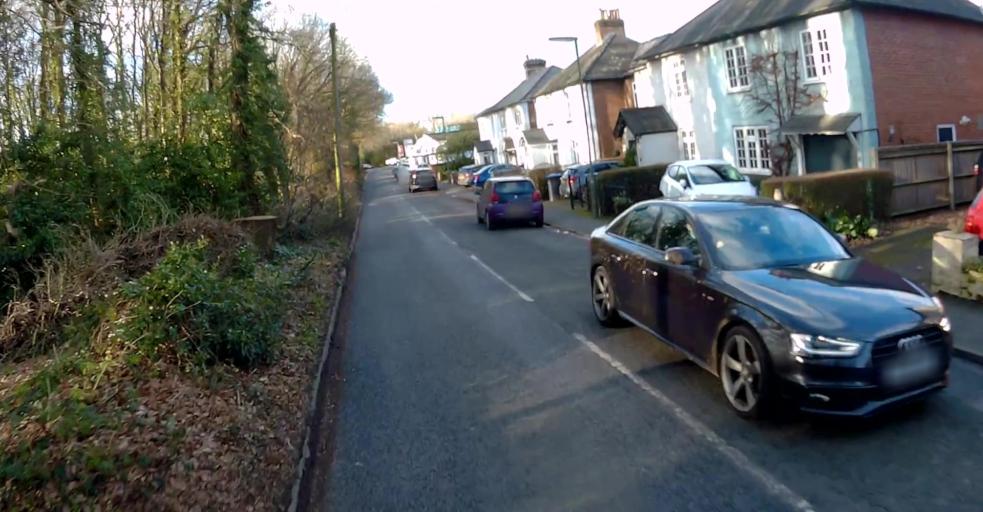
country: GB
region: England
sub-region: Surrey
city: Ottershaw
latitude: 51.3652
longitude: -0.5165
